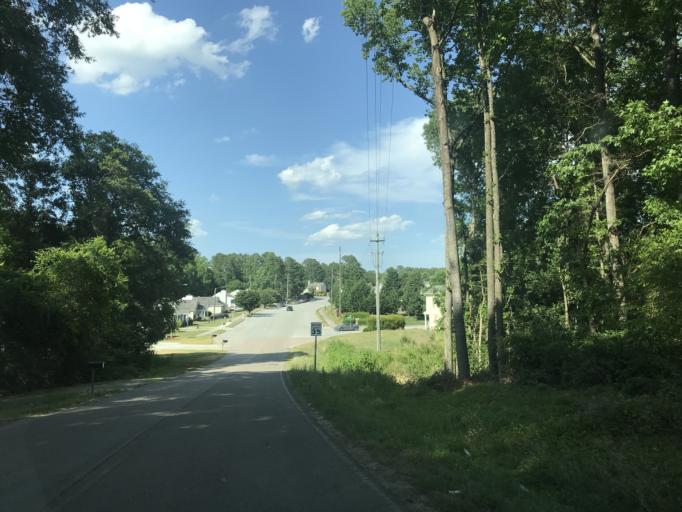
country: US
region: North Carolina
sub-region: Wake County
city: Garner
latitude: 35.7259
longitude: -78.5616
